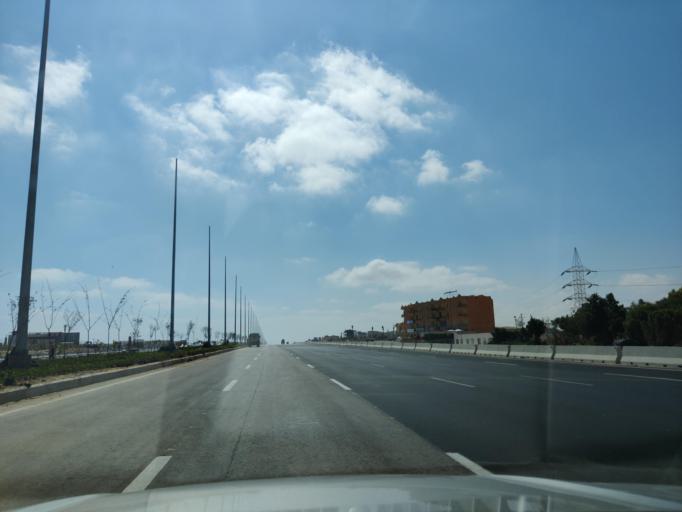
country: EG
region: Muhafazat Matruh
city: Al `Alamayn
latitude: 30.9926
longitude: 28.6709
